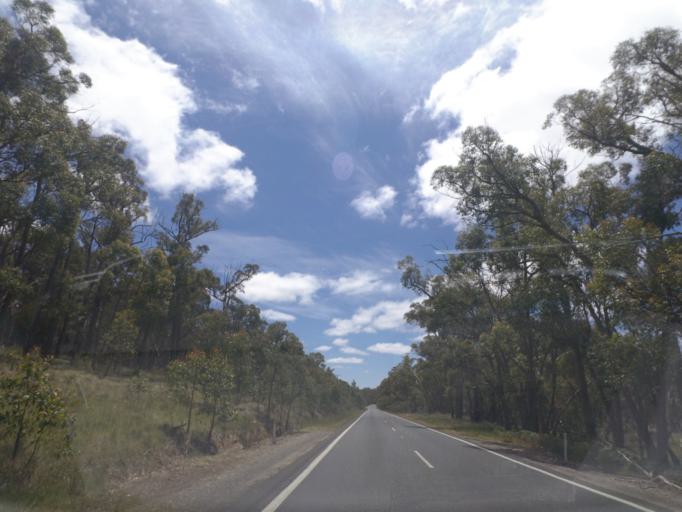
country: AU
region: Victoria
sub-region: Mount Alexander
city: Castlemaine
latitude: -37.3047
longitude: 144.1638
